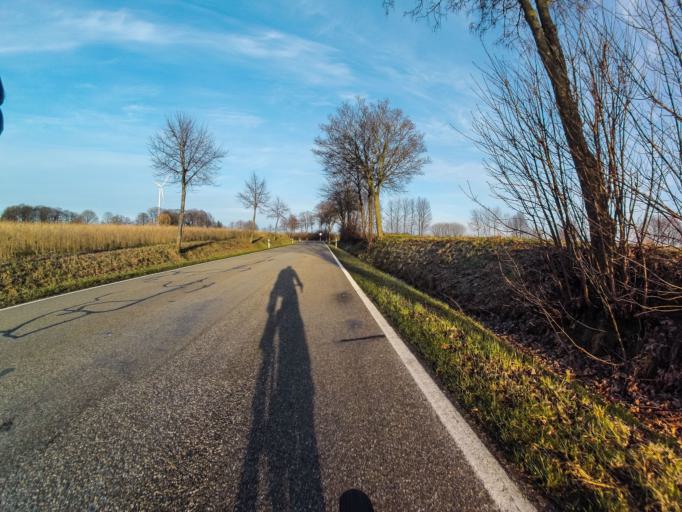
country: DE
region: North Rhine-Westphalia
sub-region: Regierungsbezirk Munster
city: Mettingen
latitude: 52.2981
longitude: 7.8304
